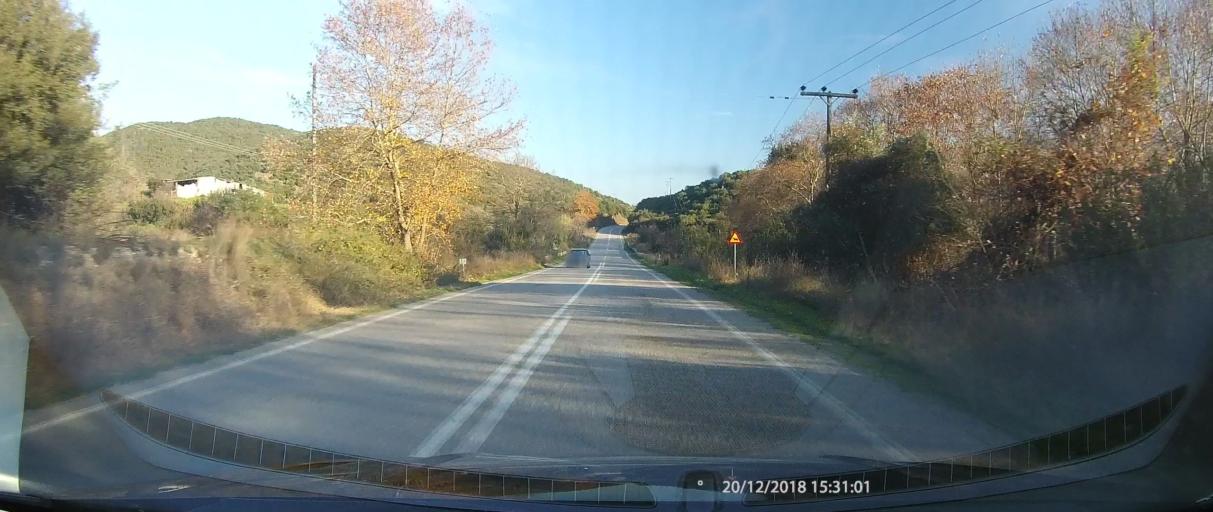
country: GR
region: Central Greece
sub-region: Nomos Fthiotidos
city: Lianokladhion
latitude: 38.9334
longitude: 22.2315
